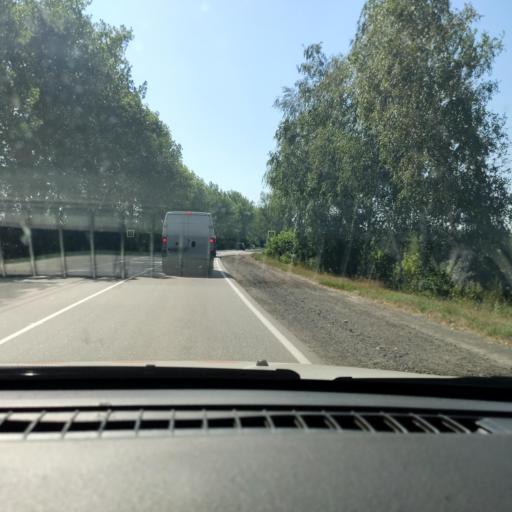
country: RU
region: Voronezj
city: Ostrogozhsk
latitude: 50.8237
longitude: 39.1567
